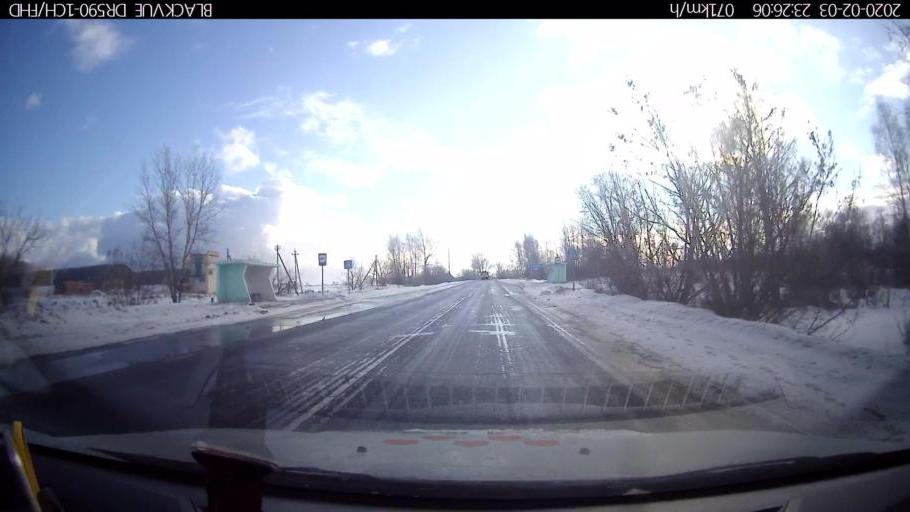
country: RU
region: Nizjnij Novgorod
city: Kstovo
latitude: 55.9963
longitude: 44.2125
